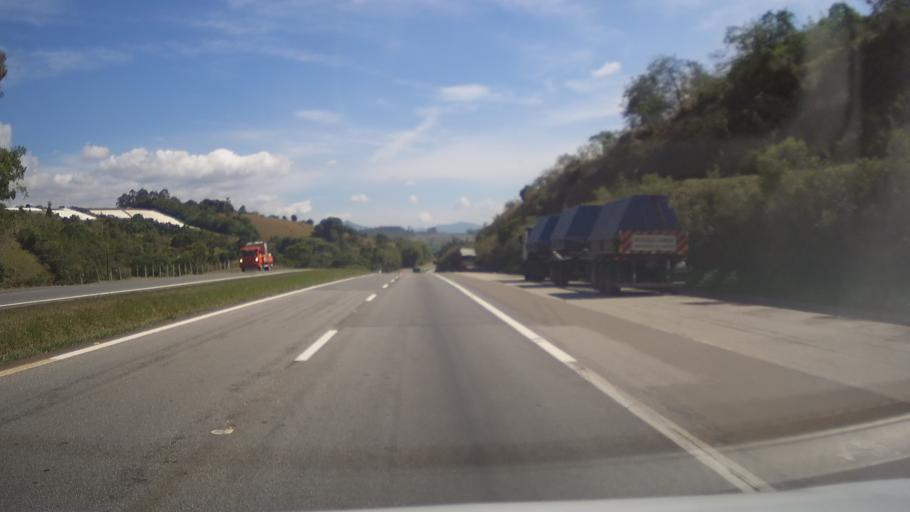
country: BR
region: Minas Gerais
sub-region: Cambui
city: Cambui
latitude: -22.5604
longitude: -46.0404
